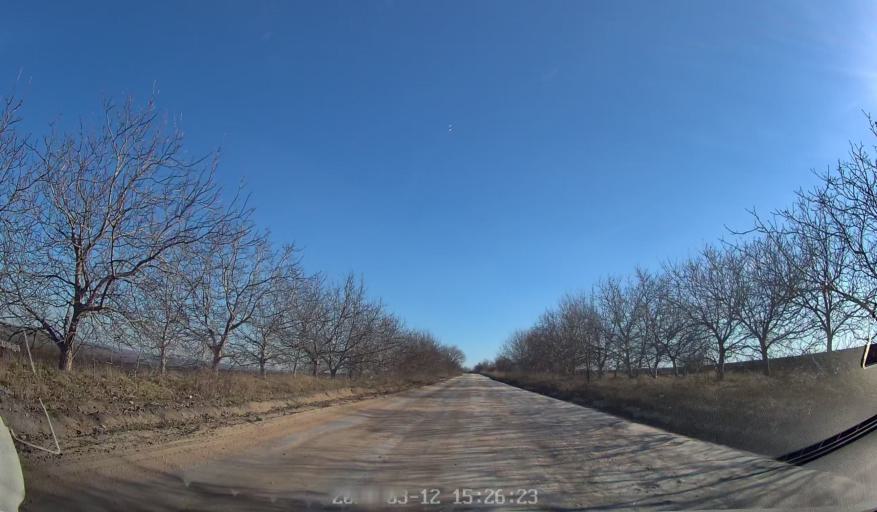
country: MD
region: Chisinau
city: Ciorescu
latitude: 47.1785
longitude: 28.9230
